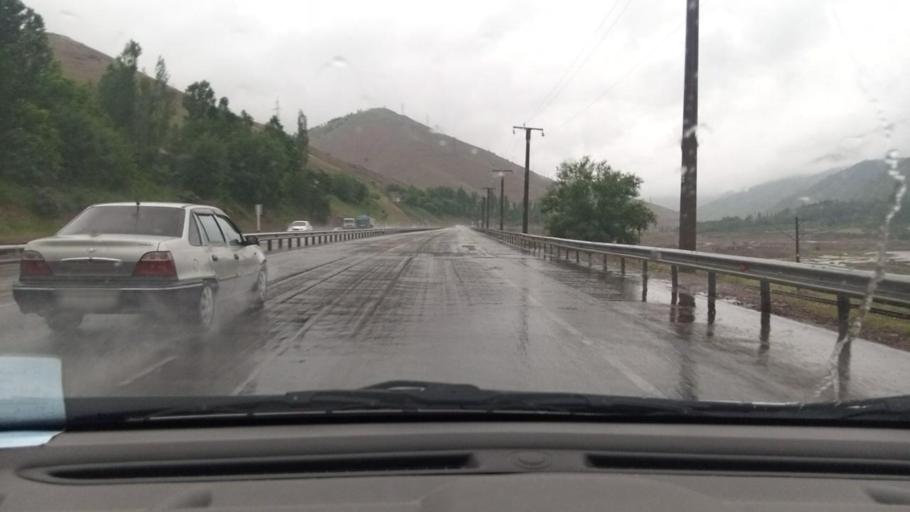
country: UZ
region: Toshkent
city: Angren
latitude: 41.1427
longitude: 70.4033
